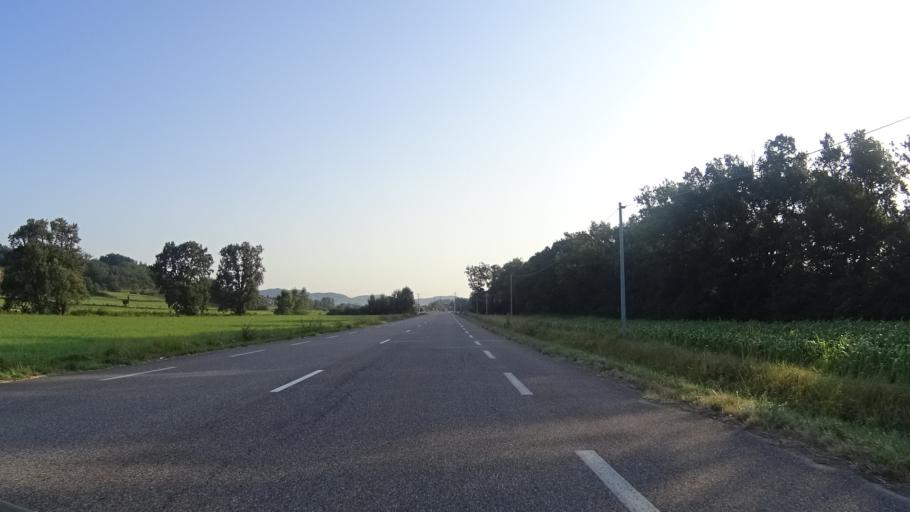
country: FR
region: Midi-Pyrenees
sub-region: Departement de l'Ariege
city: Mirepoix
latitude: 43.0251
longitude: 1.8945
